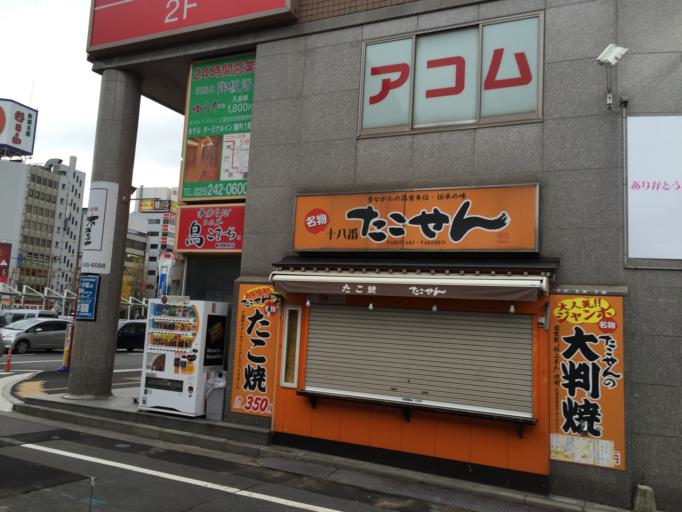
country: JP
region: Niigata
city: Niigata-shi
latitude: 37.9132
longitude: 139.0621
